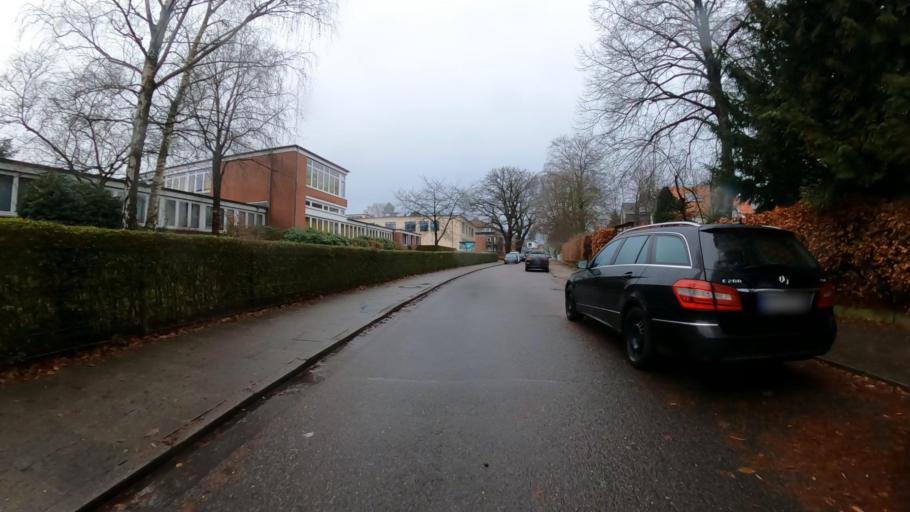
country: DE
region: Hamburg
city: Farmsen-Berne
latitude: 53.6105
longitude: 10.1596
